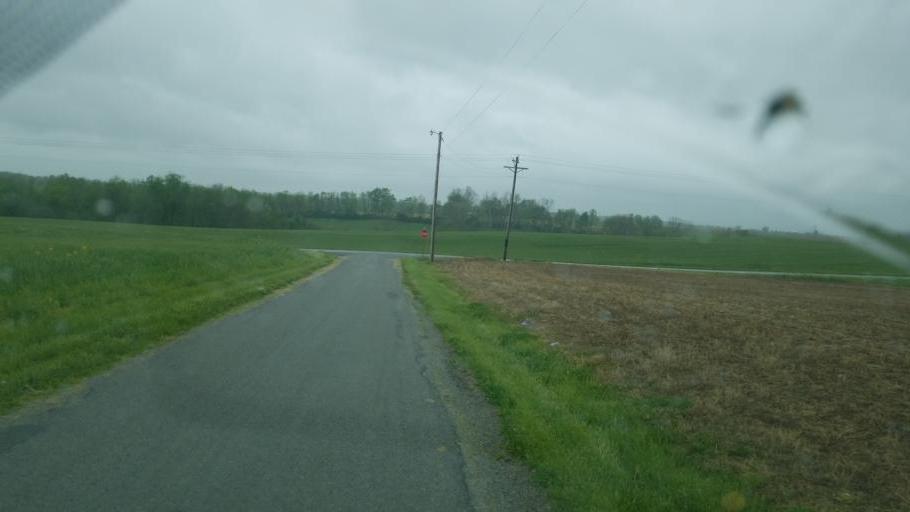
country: US
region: Ohio
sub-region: Highland County
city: Greenfield
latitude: 39.3343
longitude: -83.4577
